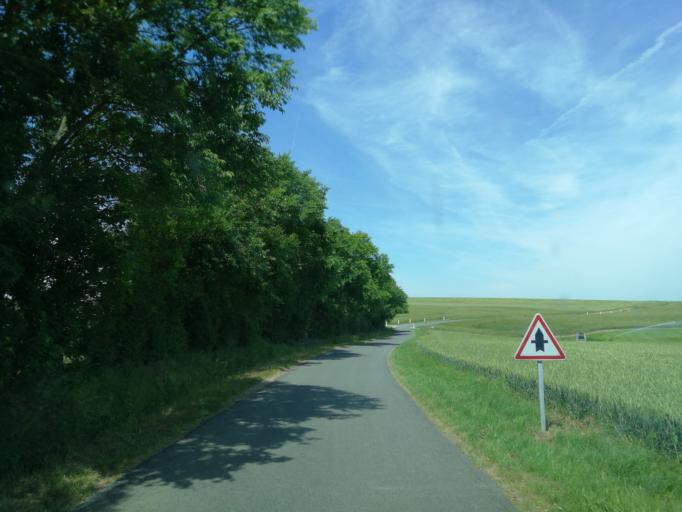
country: FR
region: Pays de la Loire
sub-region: Departement de la Vendee
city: Le Langon
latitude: 46.4343
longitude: -0.8894
